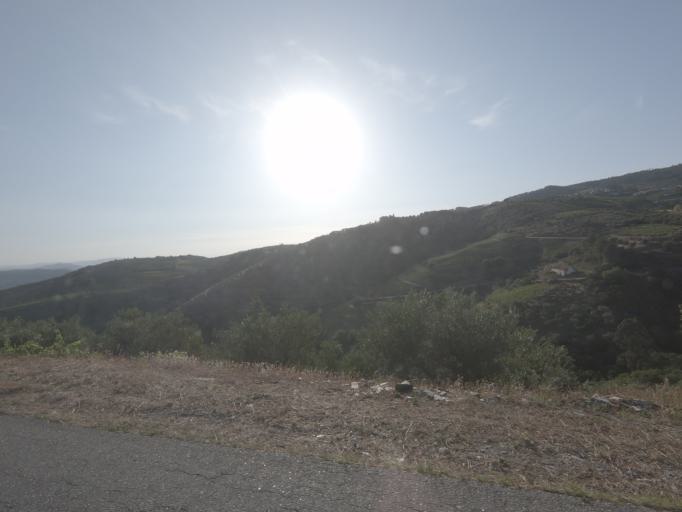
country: PT
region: Vila Real
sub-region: Sabrosa
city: Vilela
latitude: 41.1755
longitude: -7.5980
